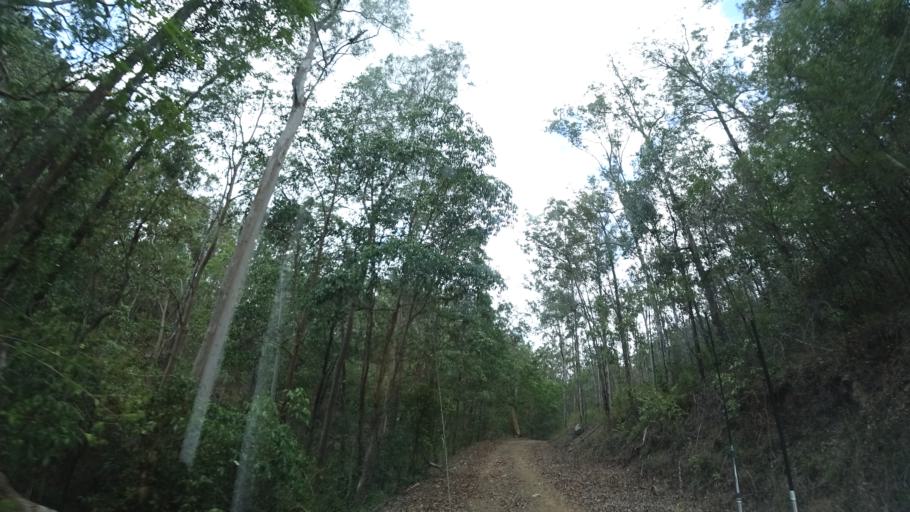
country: AU
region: Queensland
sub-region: Moreton Bay
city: Highvale
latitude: -27.3580
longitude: 152.7288
